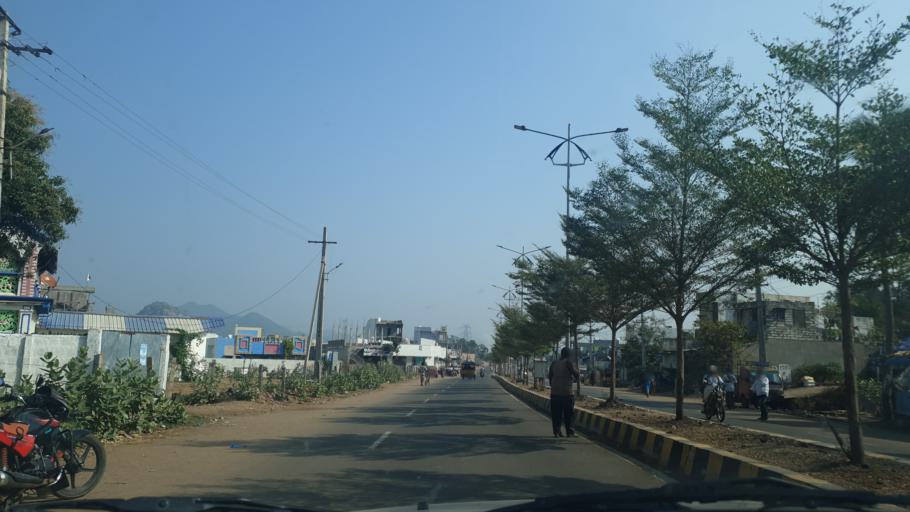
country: IN
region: Andhra Pradesh
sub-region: Srikakulam
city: Tekkali
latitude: 18.6106
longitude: 84.2332
